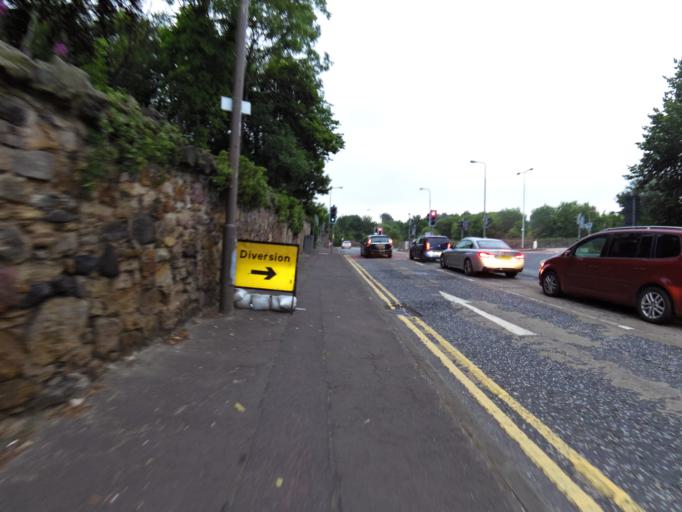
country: GB
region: Scotland
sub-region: Midlothian
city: Bonnyrigg
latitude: 55.9135
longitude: -3.1259
